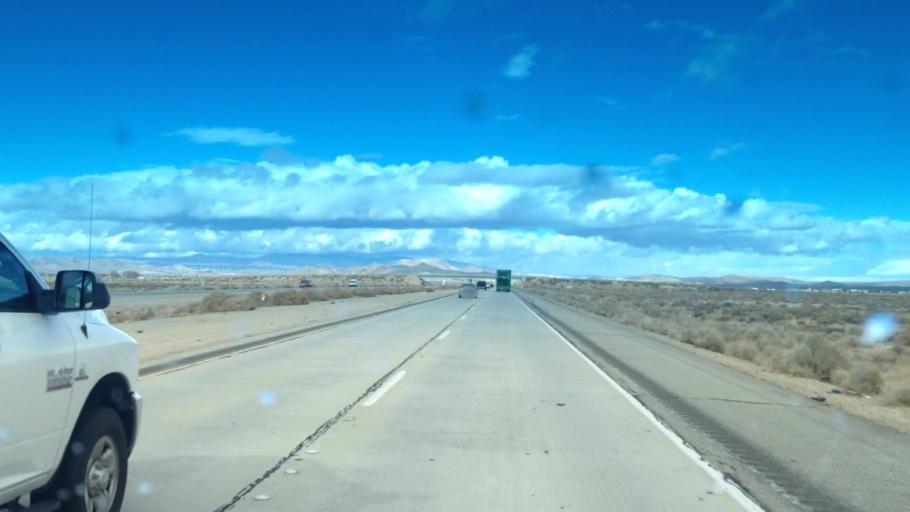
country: US
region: California
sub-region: Kern County
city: Rosamond
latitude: 34.8004
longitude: -118.1706
